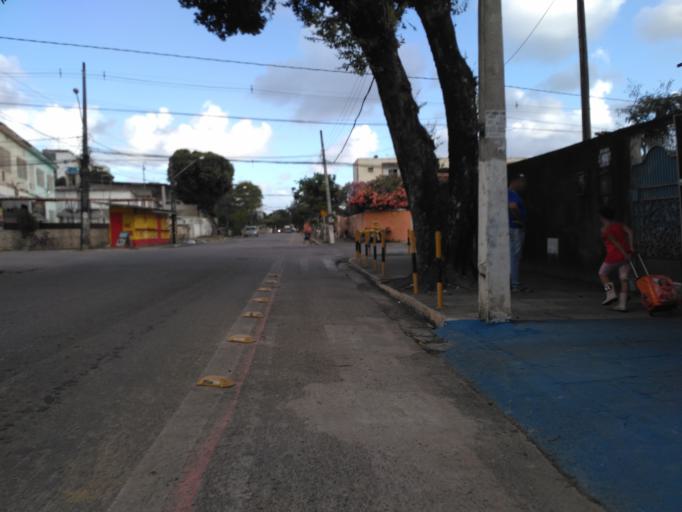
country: BR
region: Pernambuco
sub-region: Recife
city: Recife
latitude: -8.0493
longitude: -34.9410
